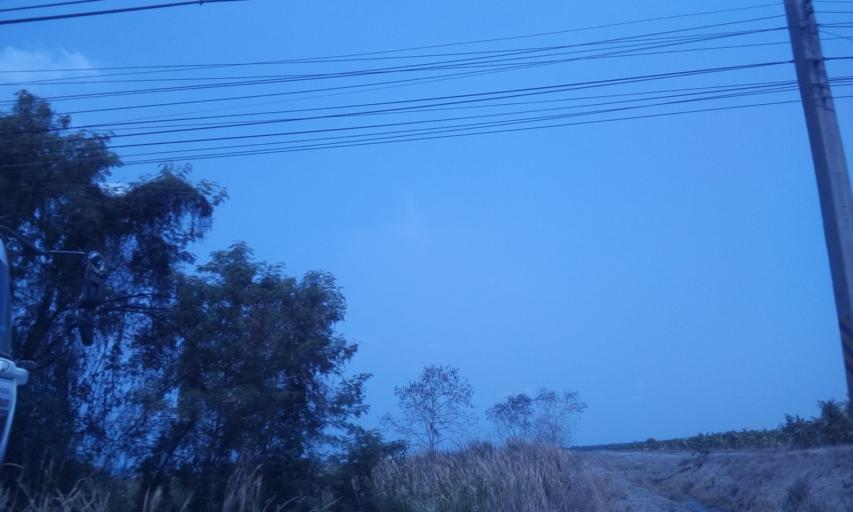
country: TH
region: Bangkok
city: Nong Chok
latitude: 13.9684
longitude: 100.9446
